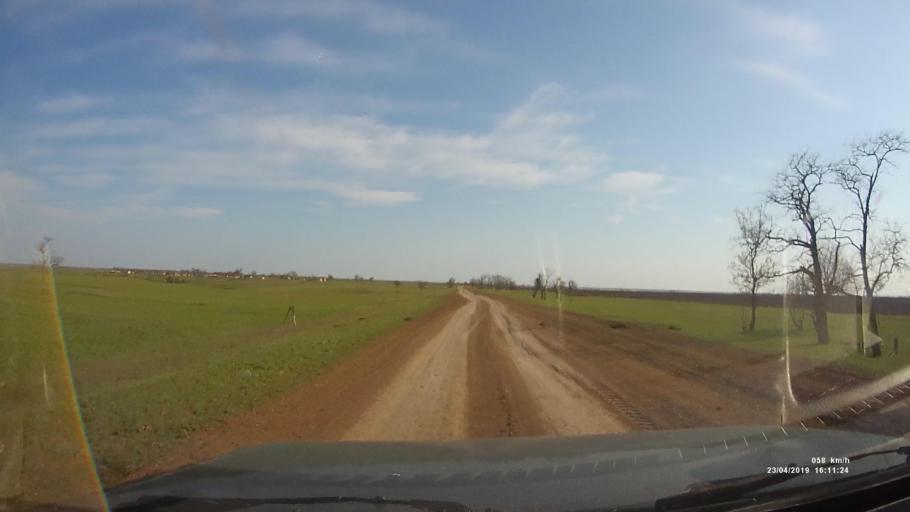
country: RU
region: Rostov
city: Remontnoye
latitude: 46.4742
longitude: 43.1231
